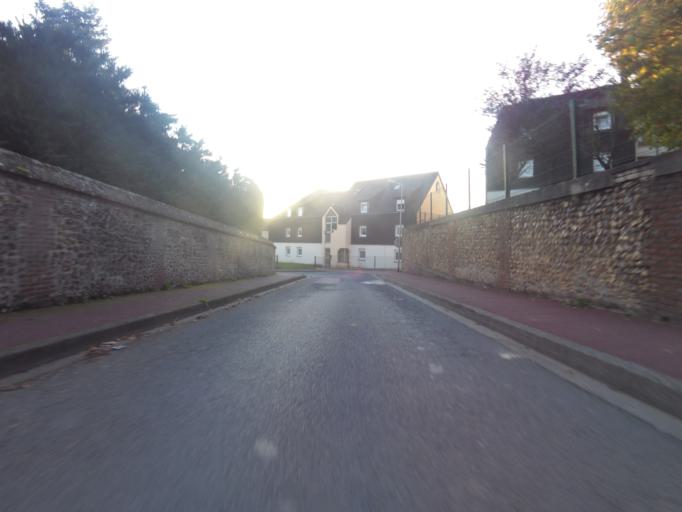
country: FR
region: Lower Normandy
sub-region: Departement du Calvados
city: La Vespiere
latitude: 49.0247
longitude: 0.4074
